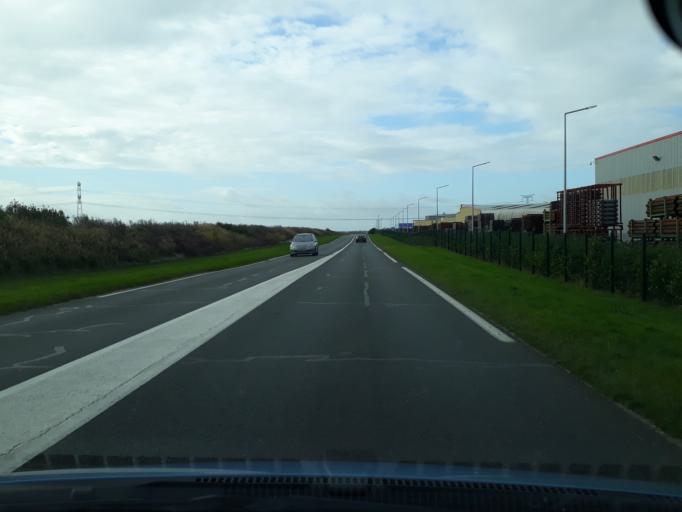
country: FR
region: Centre
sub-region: Departement du Loiret
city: Pithiviers-le-Vieil
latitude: 48.1268
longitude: 2.1953
